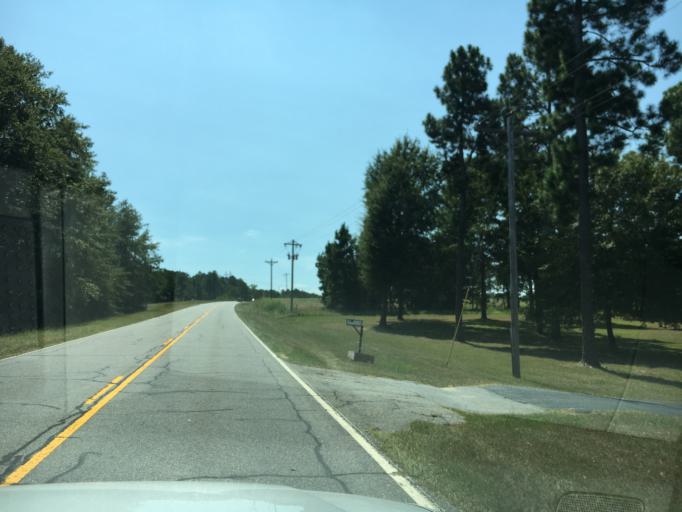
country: US
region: South Carolina
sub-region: Lexington County
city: Batesburg
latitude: 33.7762
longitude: -81.6411
